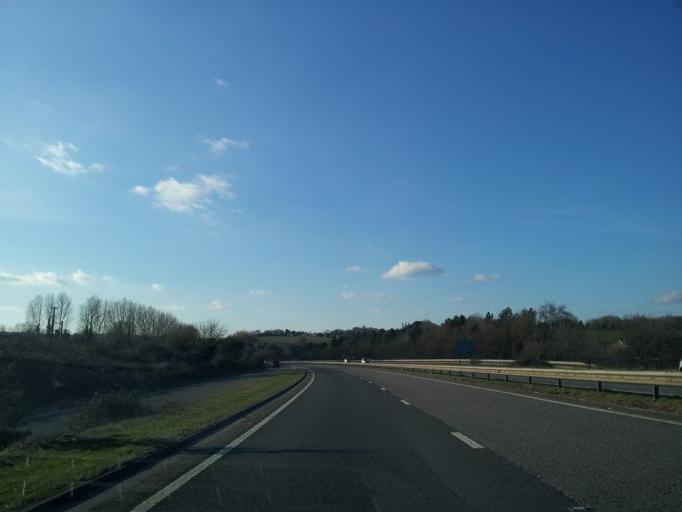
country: GB
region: England
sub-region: Devon
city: Exeter
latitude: 50.7022
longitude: -3.5460
